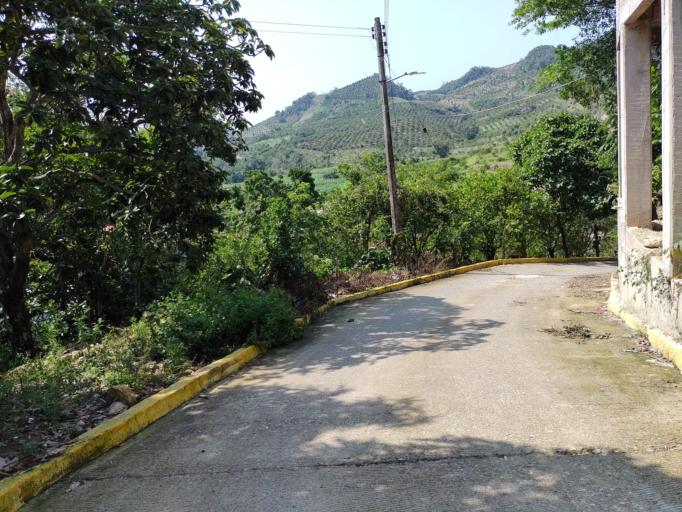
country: MX
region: Veracruz
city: Agua Dulce
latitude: 20.3105
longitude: -97.1699
